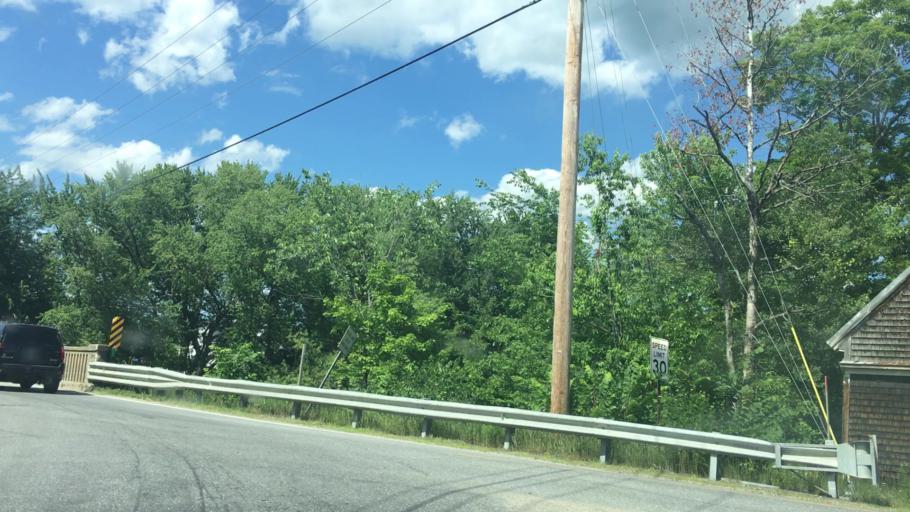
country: US
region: Maine
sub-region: Franklin County
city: New Sharon
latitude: 44.6196
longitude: -70.0746
